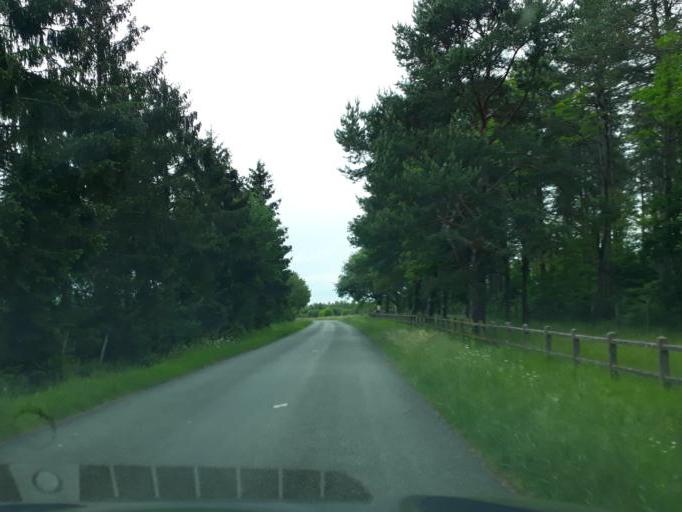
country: FR
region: Centre
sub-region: Departement du Loiret
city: Tigy
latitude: 47.7482
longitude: 2.2465
